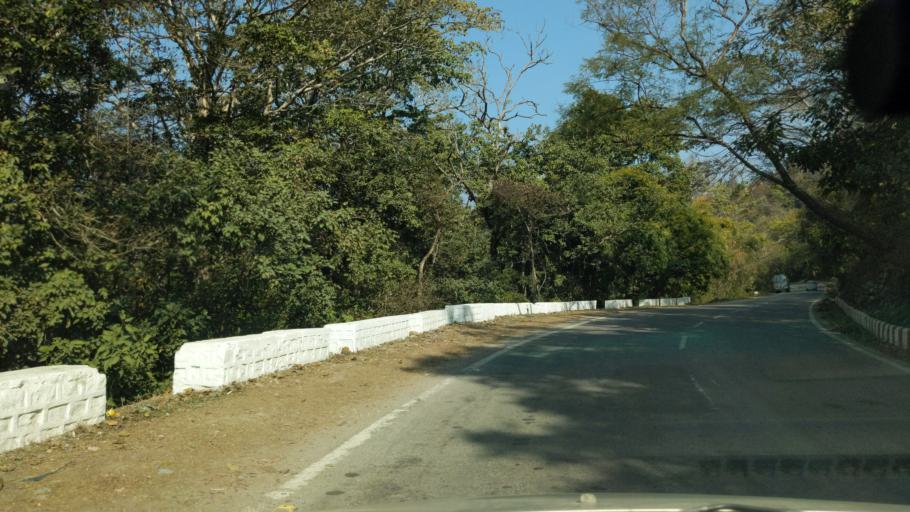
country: IN
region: Uttarakhand
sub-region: Naini Tal
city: Ramnagar
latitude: 29.3911
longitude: 79.1377
